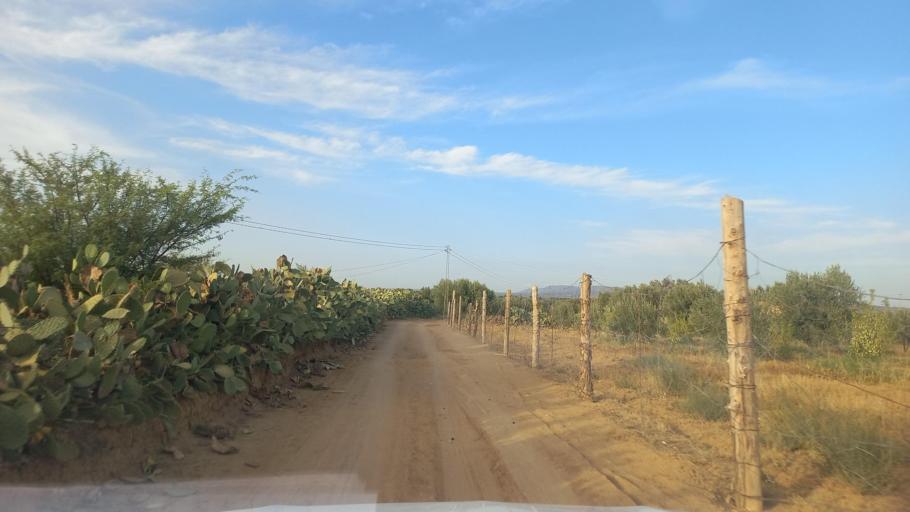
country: TN
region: Al Qasrayn
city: Kasserine
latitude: 35.2467
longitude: 9.0300
